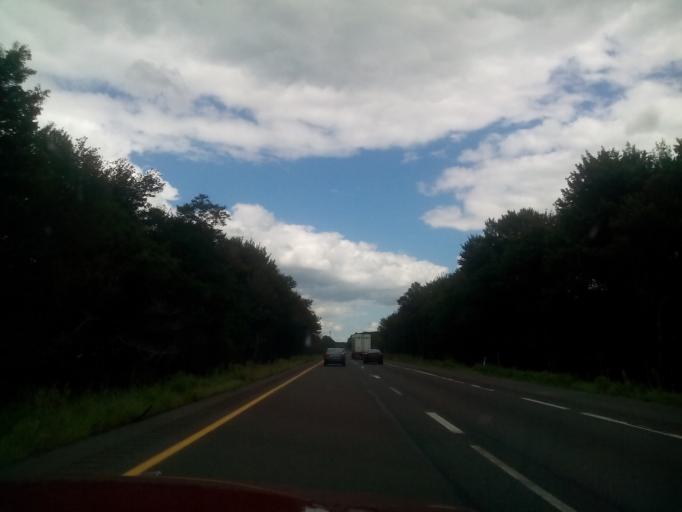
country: US
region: Pennsylvania
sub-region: Monroe County
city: Pocono Pines
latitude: 41.0733
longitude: -75.4616
